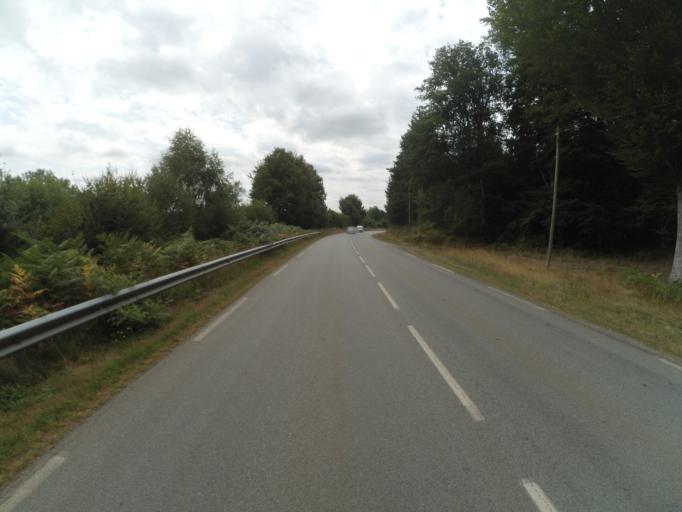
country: FR
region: Limousin
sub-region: Departement de la Correze
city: Ussel
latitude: 45.5898
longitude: 2.2917
